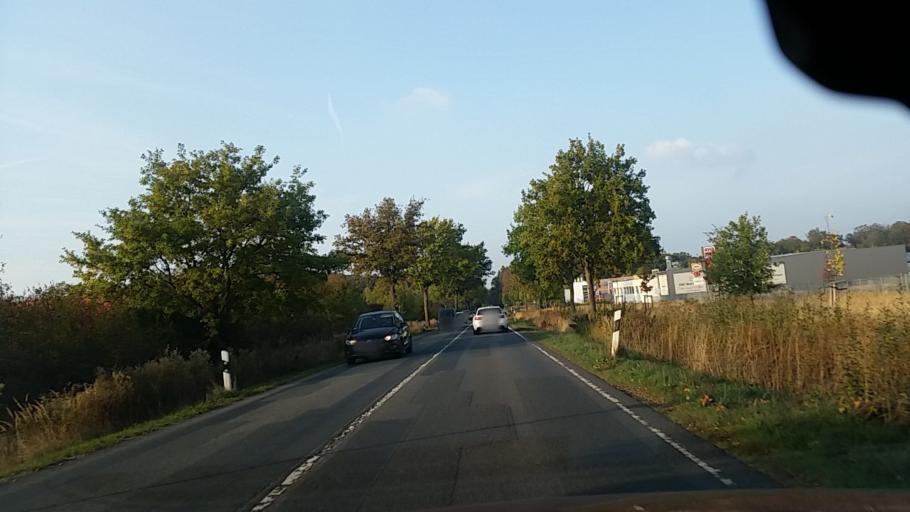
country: DE
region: Lower Saxony
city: Wolfsburg
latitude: 52.3708
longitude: 10.7454
